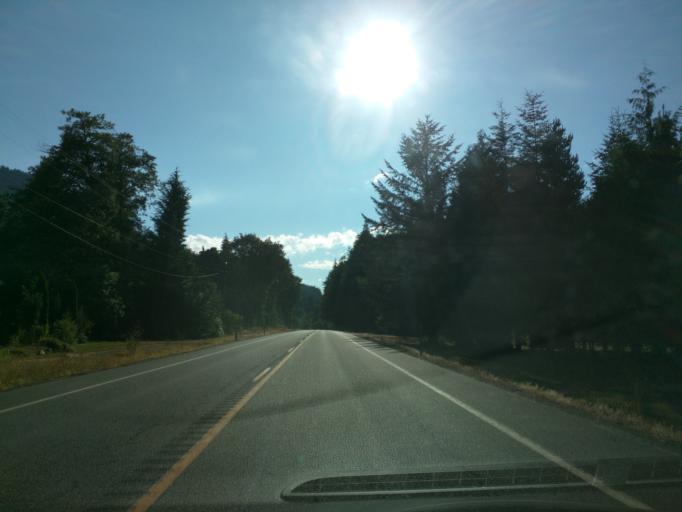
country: US
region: Washington
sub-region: Snohomish County
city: Darrington
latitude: 48.2687
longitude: -121.7196
